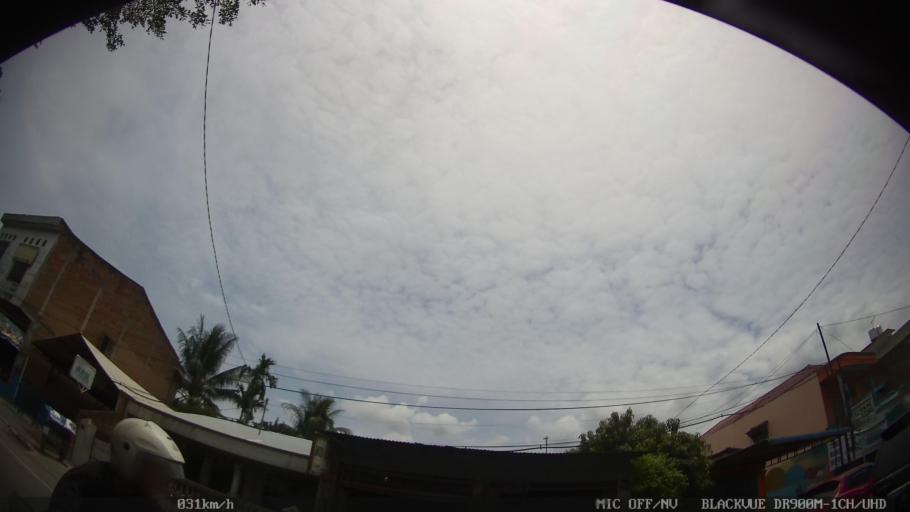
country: ID
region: North Sumatra
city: Deli Tua
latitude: 3.5289
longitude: 98.6371
